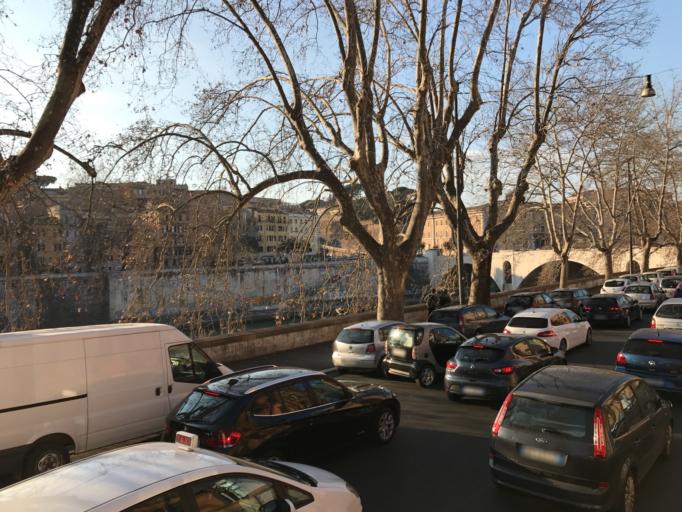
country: VA
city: Vatican City
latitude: 41.8986
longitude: 12.4647
